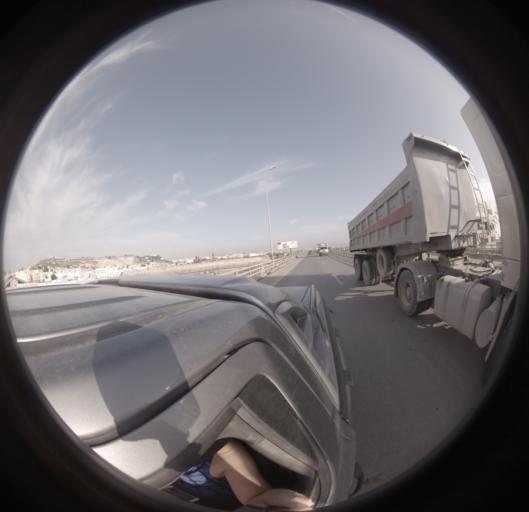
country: TN
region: Bin 'Arus
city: Ben Arous
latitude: 36.7810
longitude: 10.1972
